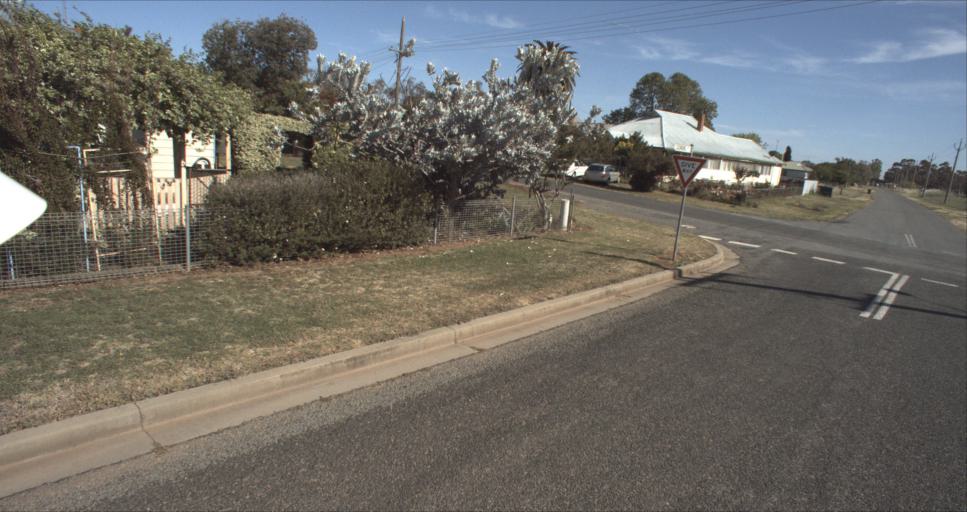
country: AU
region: New South Wales
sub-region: Leeton
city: Leeton
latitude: -34.6025
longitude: 146.4123
